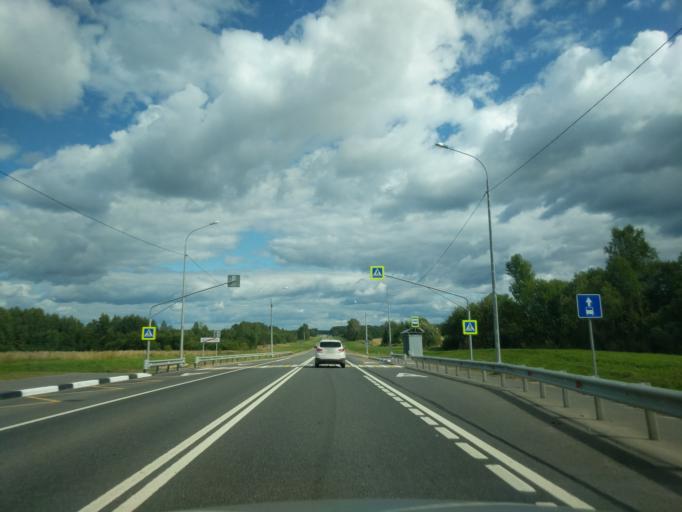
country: RU
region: Kostroma
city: Oktyabr'skiy
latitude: 57.7978
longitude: 41.2071
